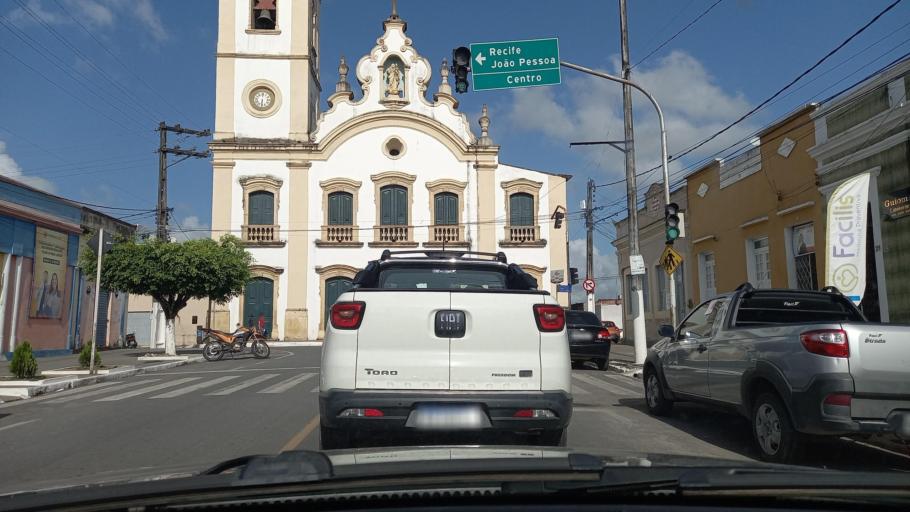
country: BR
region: Pernambuco
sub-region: Goiana
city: Goiana
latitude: -7.5589
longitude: -34.9975
